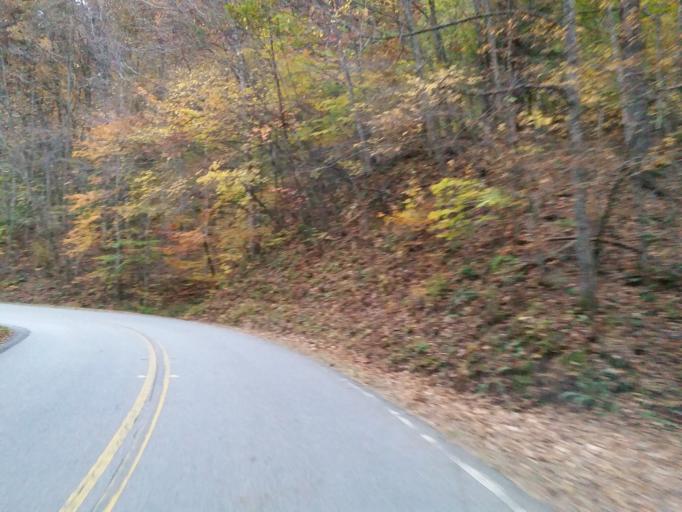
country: US
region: Georgia
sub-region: Lumpkin County
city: Dahlonega
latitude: 34.7024
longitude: -84.0458
